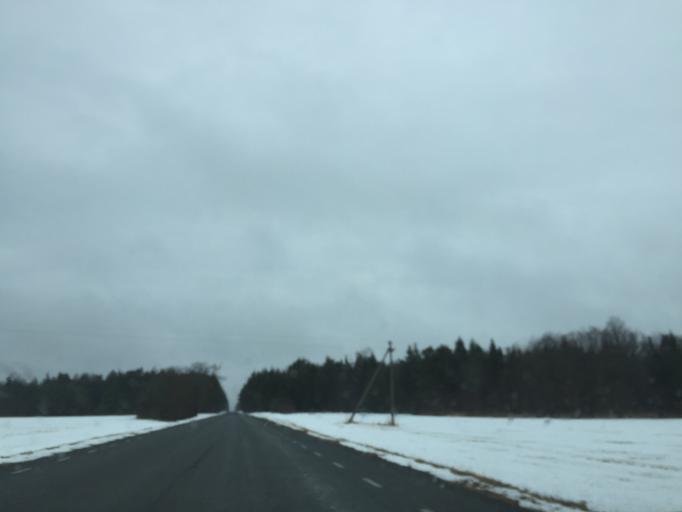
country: EE
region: Saare
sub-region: Kuressaare linn
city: Kuressaare
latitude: 58.3313
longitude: 22.0257
